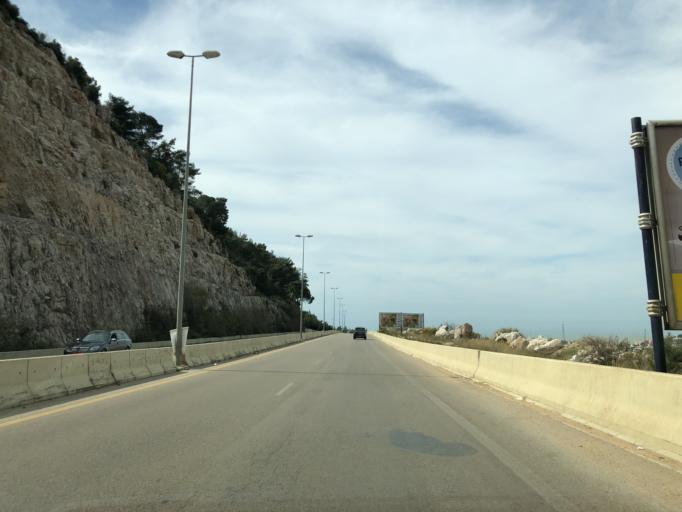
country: LB
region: Mont-Liban
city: Jdaidet el Matn
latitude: 33.8995
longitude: 35.6457
